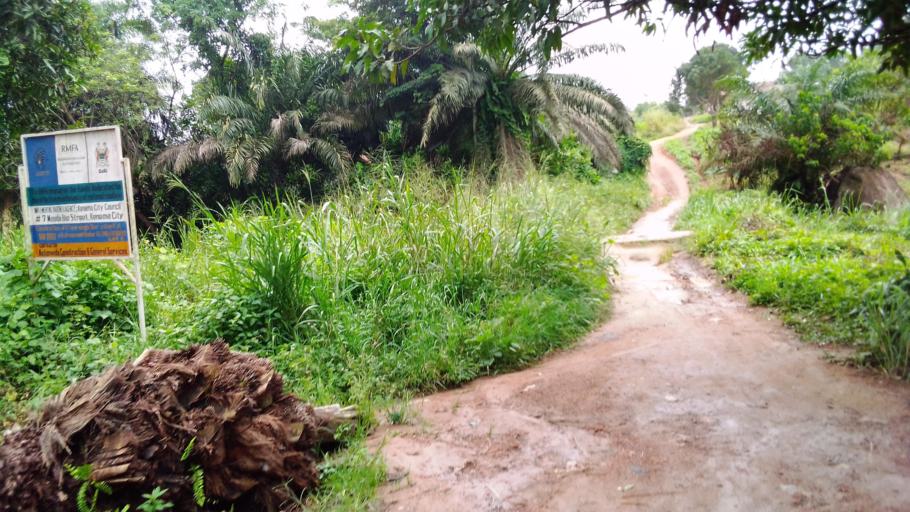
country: SL
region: Eastern Province
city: Kenema
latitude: 7.8747
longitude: -11.1704
